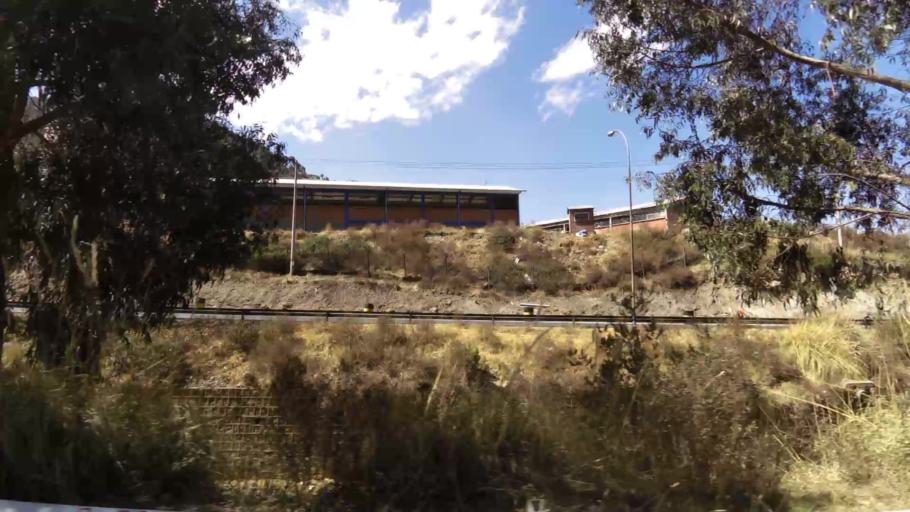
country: BO
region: La Paz
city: La Paz
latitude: -16.4744
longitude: -68.1529
